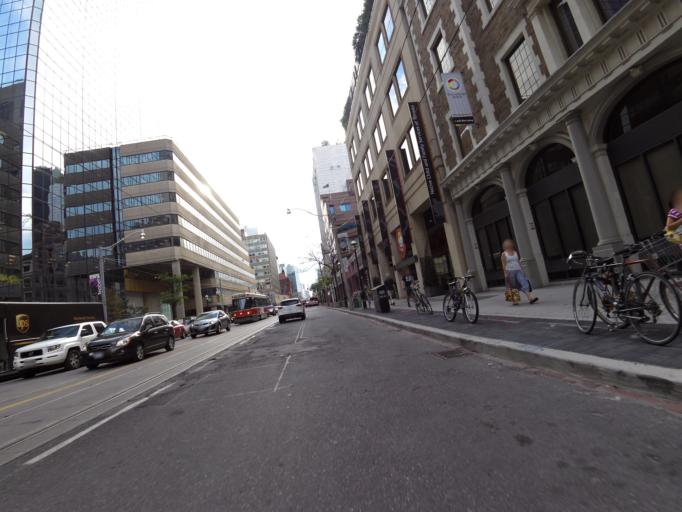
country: CA
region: Ontario
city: Toronto
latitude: 43.6612
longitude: -79.3840
